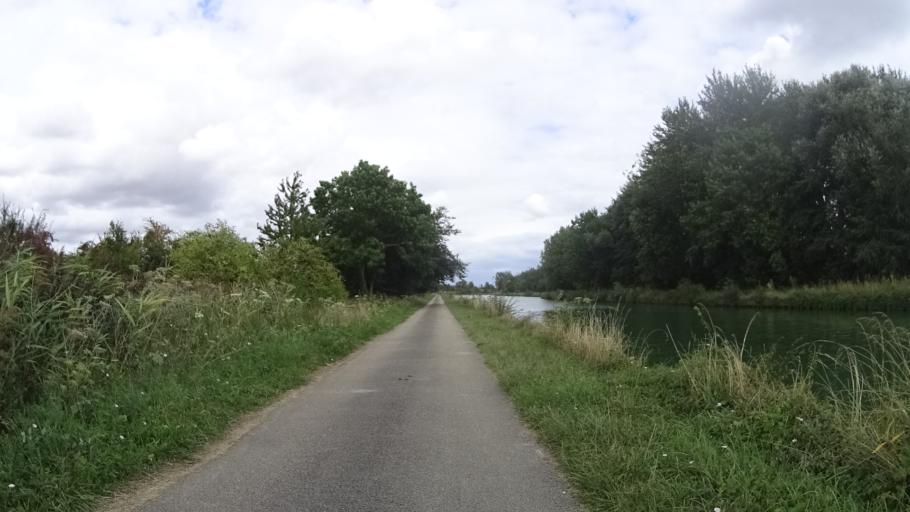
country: FR
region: Picardie
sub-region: Departement de l'Aisne
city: Tergnier
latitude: 49.6481
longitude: 3.2996
